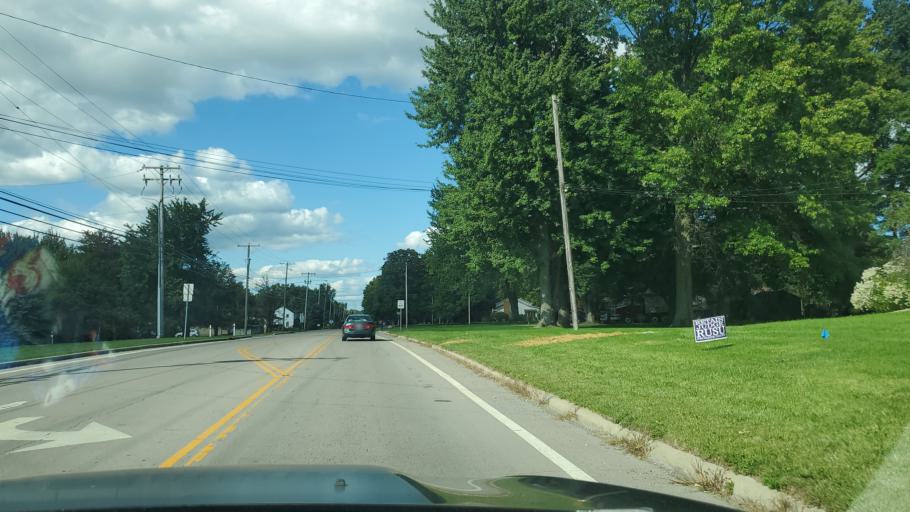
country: US
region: Ohio
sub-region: Mahoning County
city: Canfield
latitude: 41.0446
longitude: -80.7606
